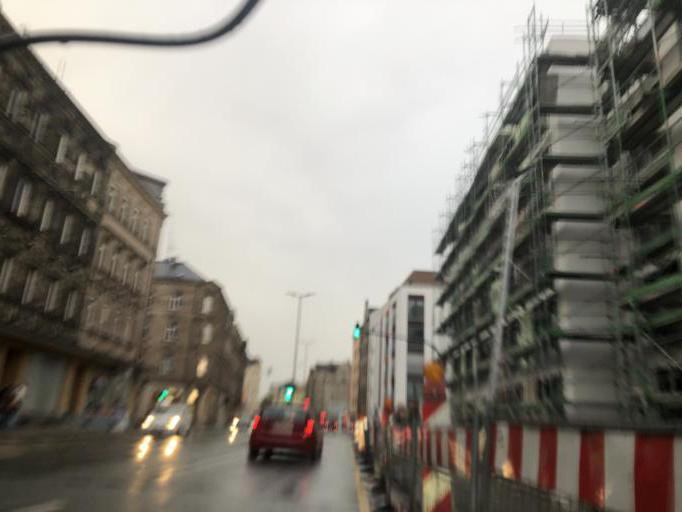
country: DE
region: Bavaria
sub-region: Regierungsbezirk Mittelfranken
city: Furth
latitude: 49.4652
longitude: 10.9858
